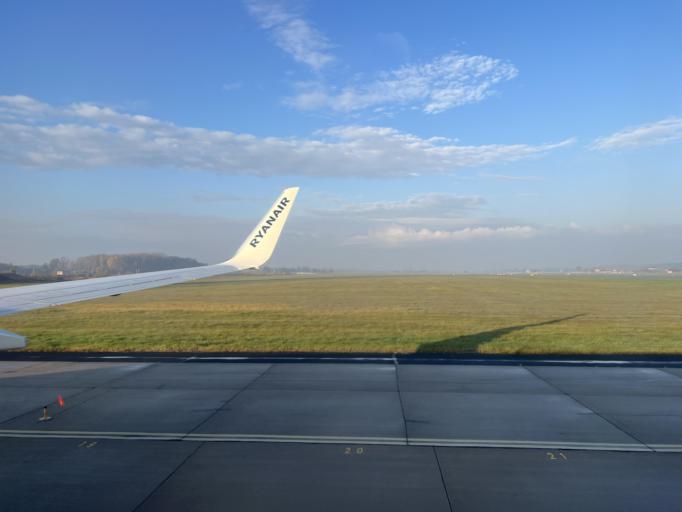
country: PL
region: Silesian Voivodeship
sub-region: Powiat tarnogorski
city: Ozarowice
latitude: 50.4731
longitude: 19.0663
